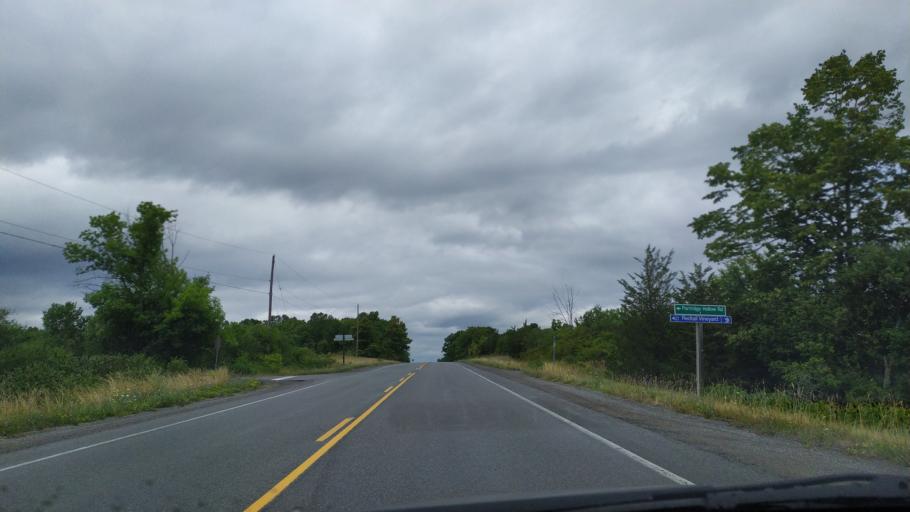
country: CA
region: Ontario
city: Quinte West
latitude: 43.9701
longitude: -77.5027
